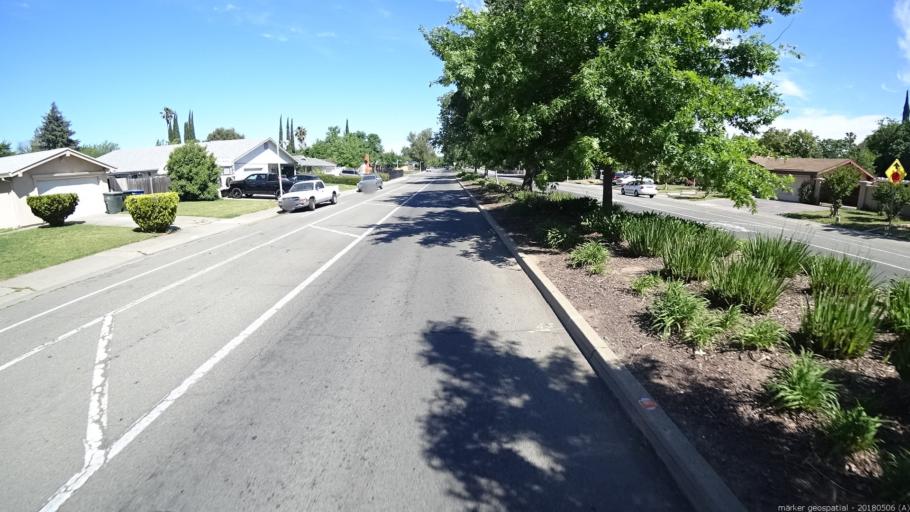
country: US
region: California
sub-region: Sacramento County
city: Parkway
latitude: 38.4766
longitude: -121.4382
